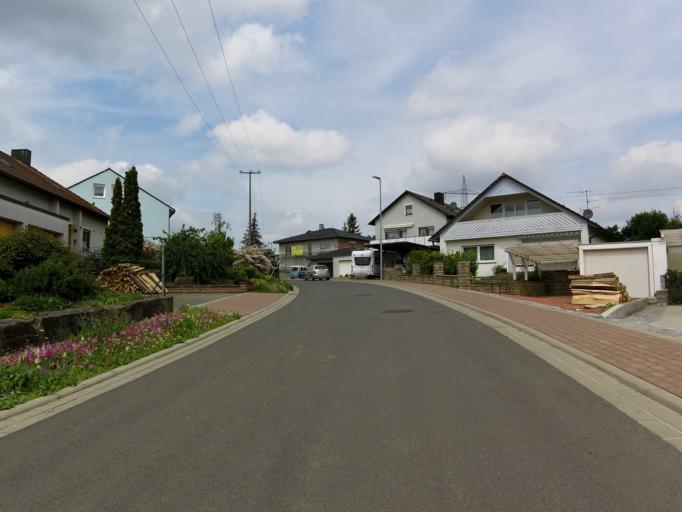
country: DE
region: Bavaria
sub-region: Regierungsbezirk Unterfranken
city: Waldbrunn
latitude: 49.7622
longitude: 9.8018
